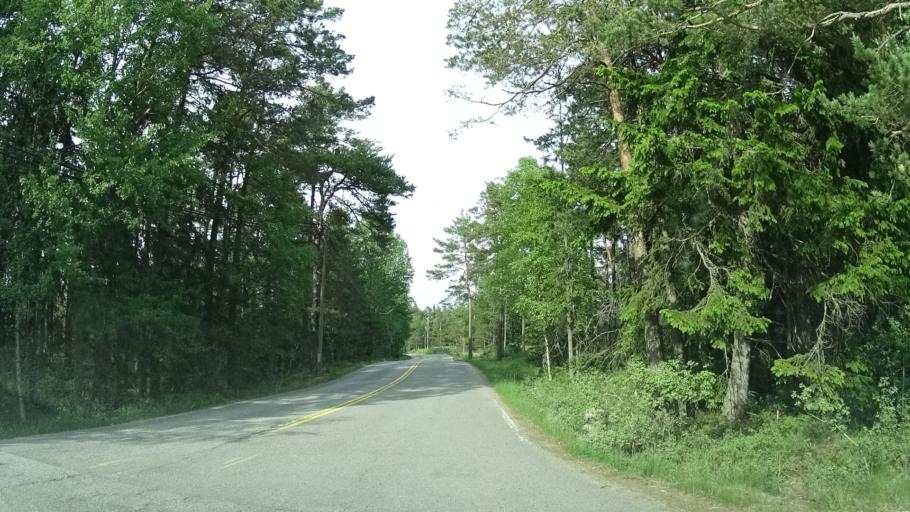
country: FI
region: Uusimaa
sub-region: Helsinki
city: Kirkkonummi
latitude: 59.9875
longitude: 24.4303
